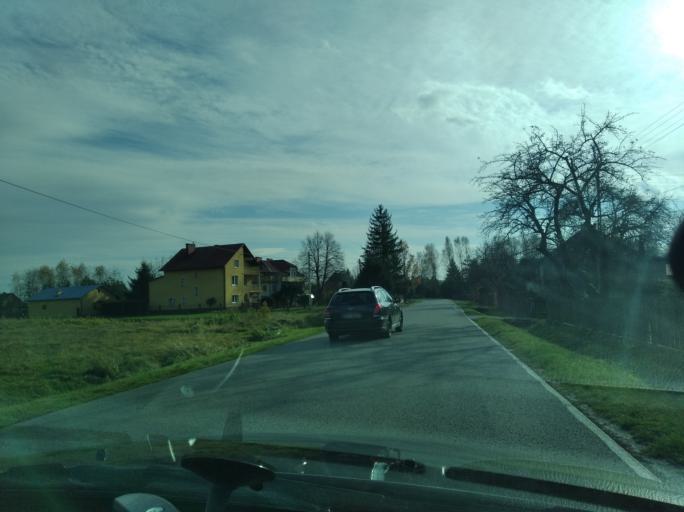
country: PL
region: Subcarpathian Voivodeship
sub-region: Powiat ropczycko-sedziszowski
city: Sedziszow Malopolski
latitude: 50.0916
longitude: 21.7441
